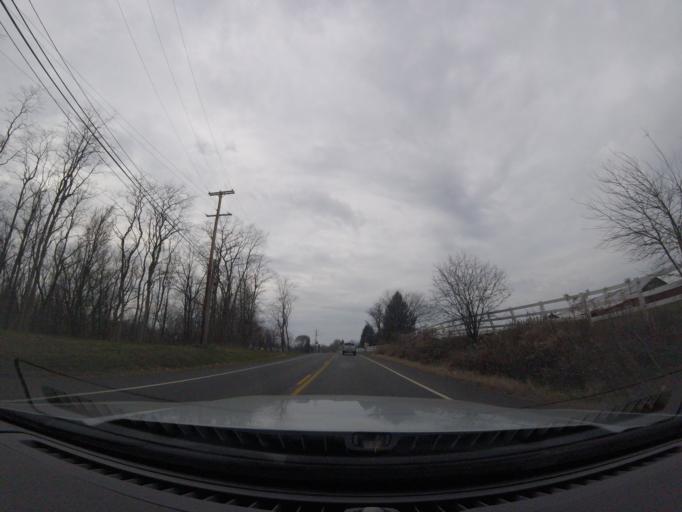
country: US
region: New York
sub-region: Schuyler County
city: Watkins Glen
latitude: 42.4218
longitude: -76.8378
